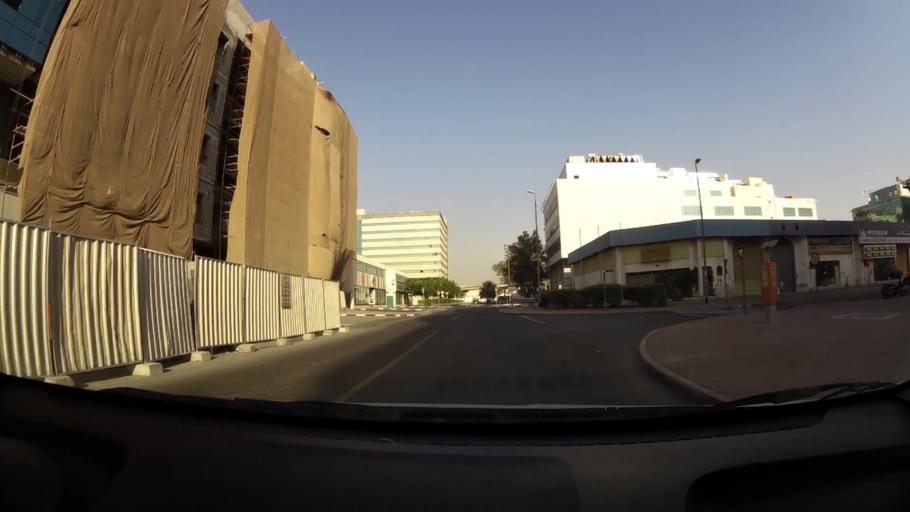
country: AE
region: Ash Shariqah
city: Sharjah
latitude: 25.2519
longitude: 55.3426
